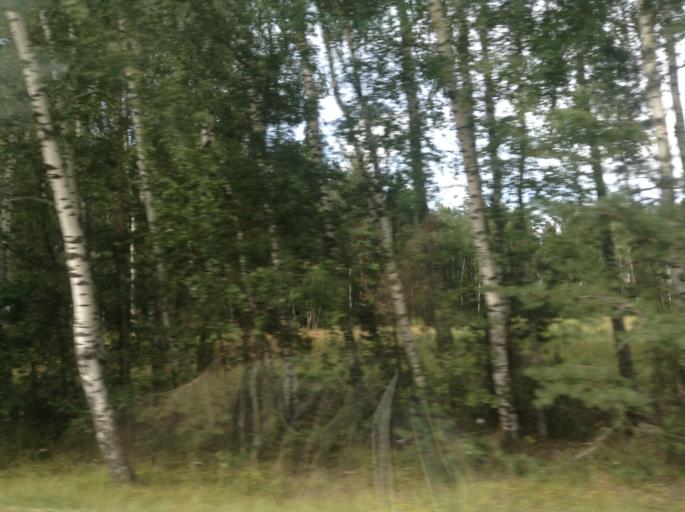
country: RU
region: Moskovskaya
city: Yegor'yevsk
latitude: 55.3587
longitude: 39.1142
